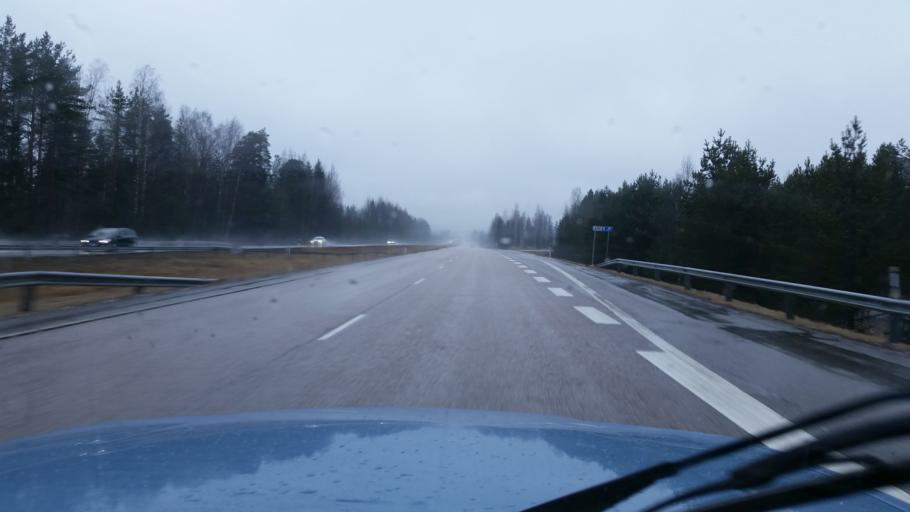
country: FI
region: Uusimaa
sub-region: Helsinki
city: Nurmijaervi
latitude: 60.5021
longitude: 24.8509
